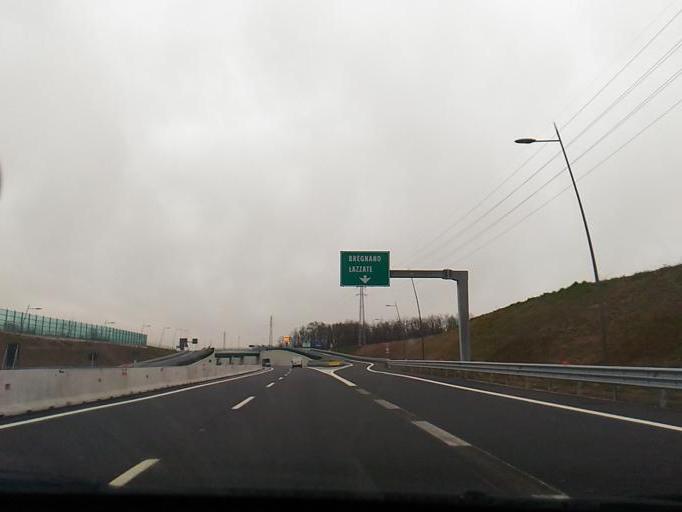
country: IT
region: Lombardy
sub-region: Provincia di Como
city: Rovellasca
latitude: 45.6787
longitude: 9.0597
